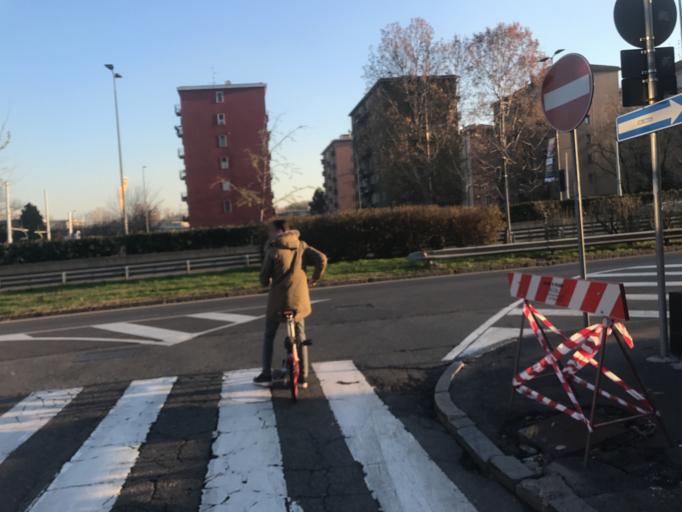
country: IT
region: Lombardy
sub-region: Citta metropolitana di Milano
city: Sesto San Giovanni
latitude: 45.4982
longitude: 9.2382
